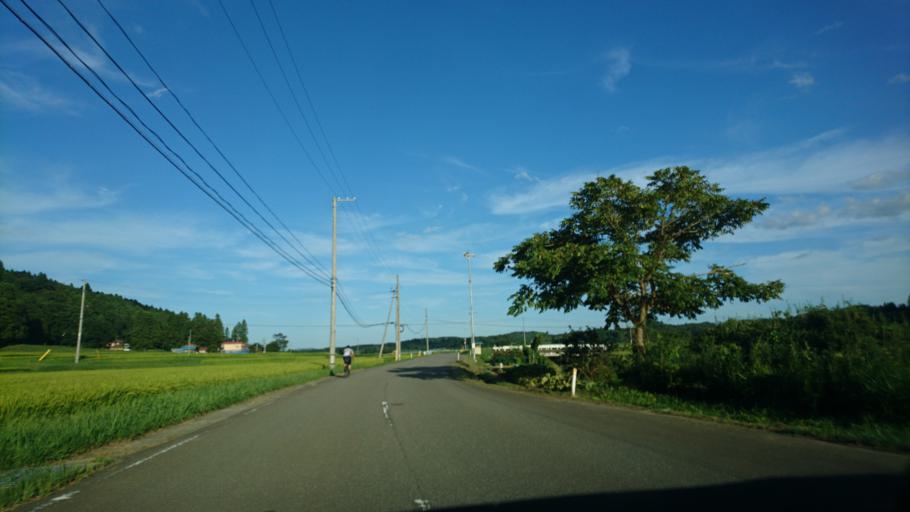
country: JP
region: Iwate
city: Ichinoseki
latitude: 38.8436
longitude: 141.1252
